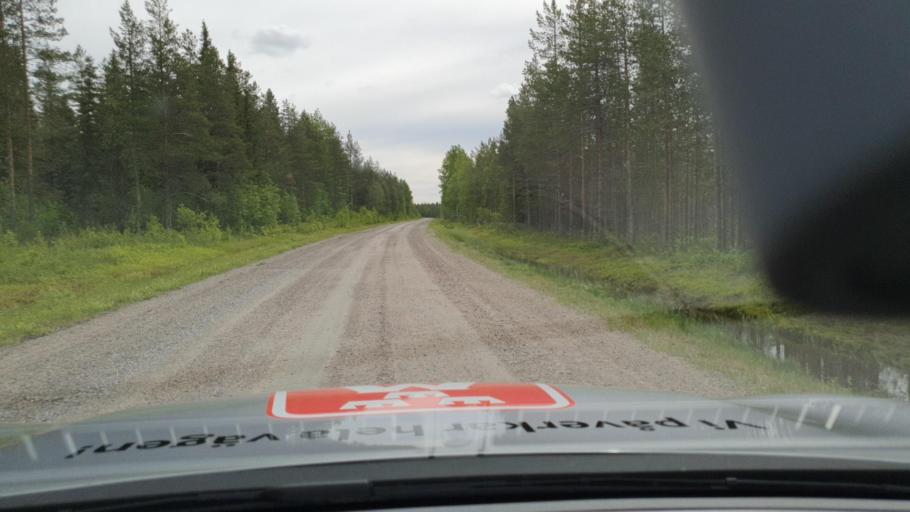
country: FI
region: Lapland
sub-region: Torniolaakso
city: Ylitornio
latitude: 65.9548
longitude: 23.7561
